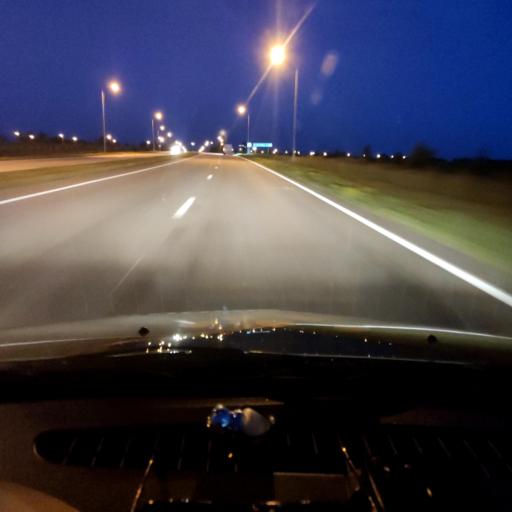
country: RU
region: Belgorod
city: Skorodnoye
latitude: 51.0608
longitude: 37.2027
